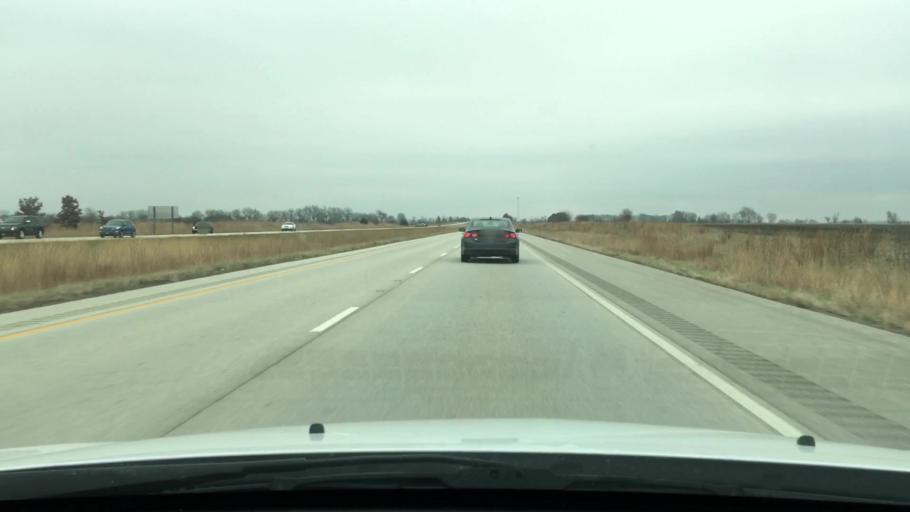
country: US
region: Illinois
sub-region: Sangamon County
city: New Berlin
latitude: 39.7403
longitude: -89.8955
